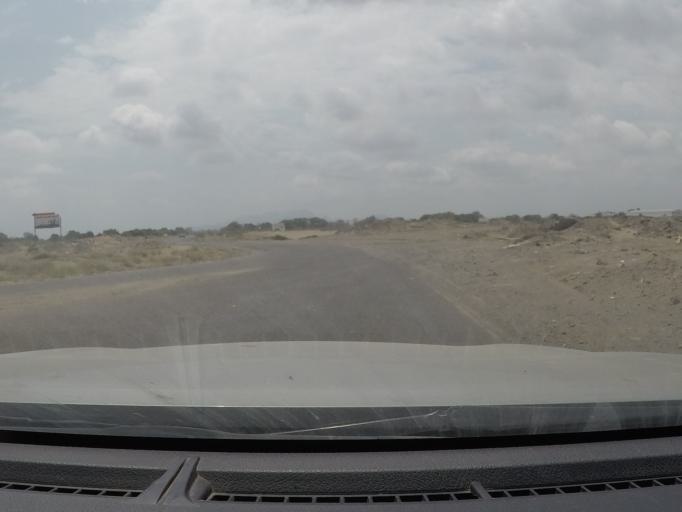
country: YE
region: Aden
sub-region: Ash Shaikh Outhman
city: Ash Shaykh `Uthman
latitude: 12.9200
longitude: 45.0082
